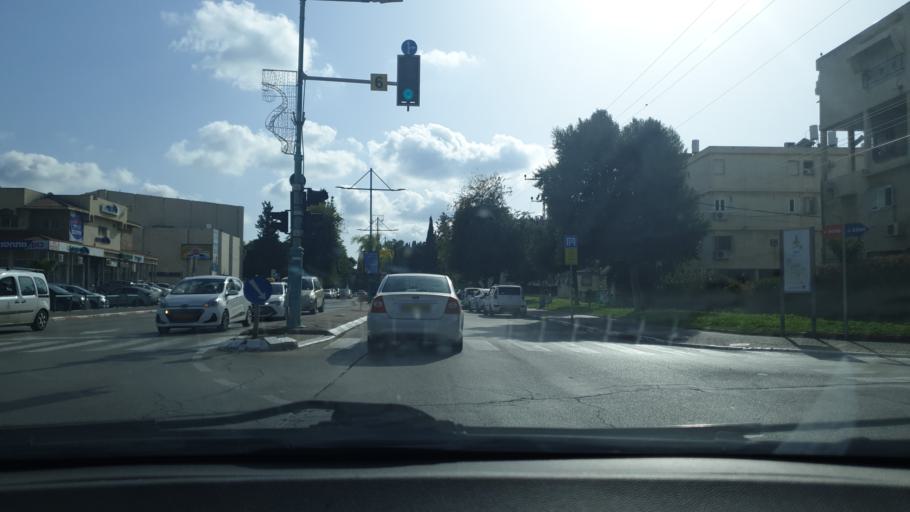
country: IL
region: Central District
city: Ramla
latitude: 31.9299
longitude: 34.8660
